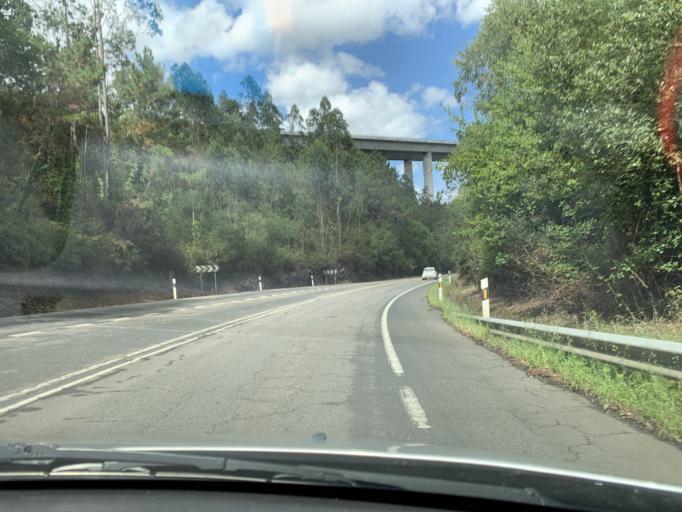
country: ES
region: Galicia
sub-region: Provincia de Lugo
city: Barreiros
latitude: 43.5029
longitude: -7.2712
